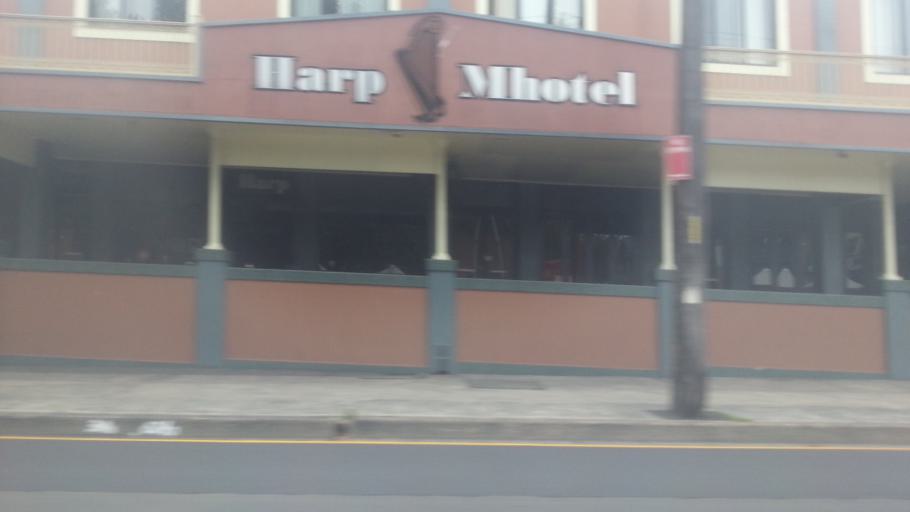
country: AU
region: New South Wales
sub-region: Wollongong
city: Wollongong
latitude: -34.4253
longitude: 150.8999
